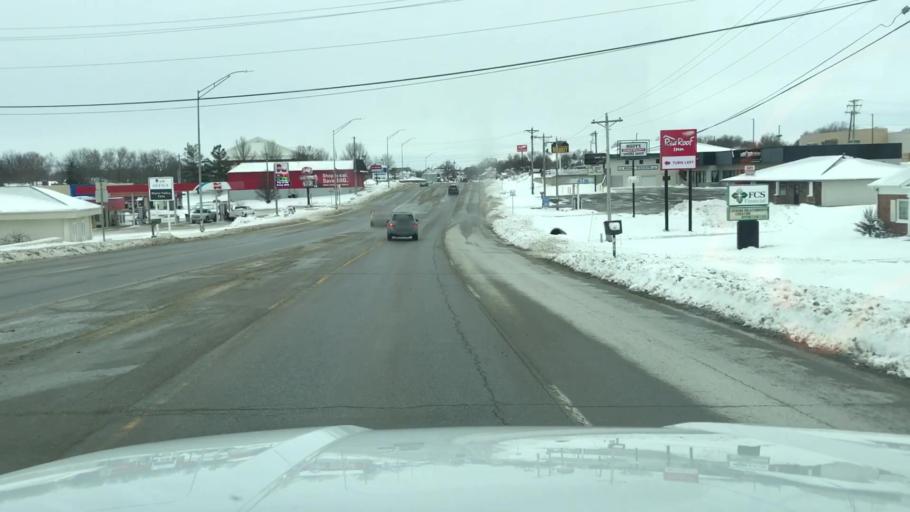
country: US
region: Missouri
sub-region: Clinton County
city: Cameron
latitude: 39.7521
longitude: -94.2344
